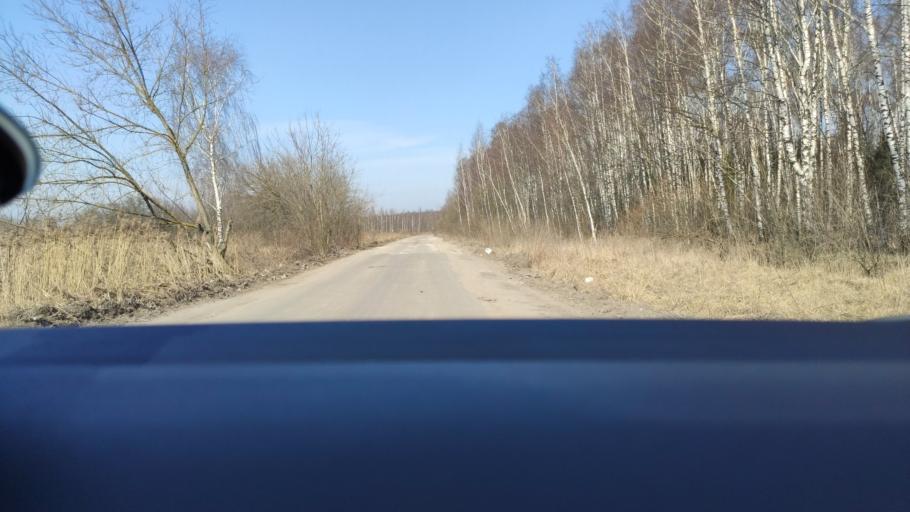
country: RU
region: Moskovskaya
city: Elektrostal'
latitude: 55.7691
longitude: 38.3845
